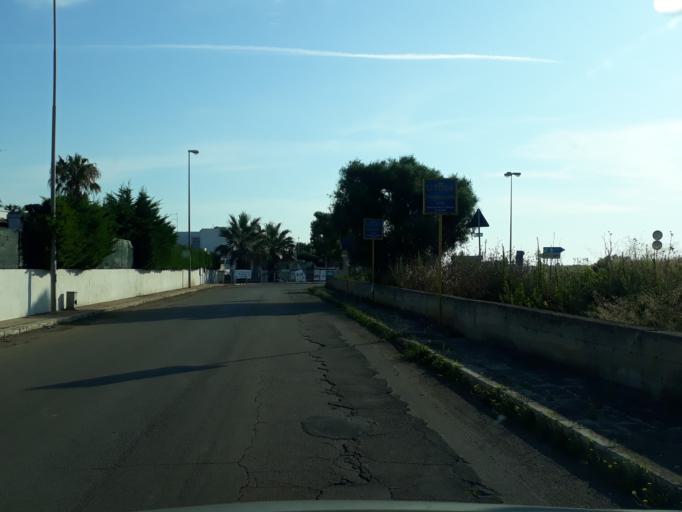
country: IT
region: Apulia
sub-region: Provincia di Brindisi
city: Carovigno
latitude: 40.7531
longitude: 17.6979
